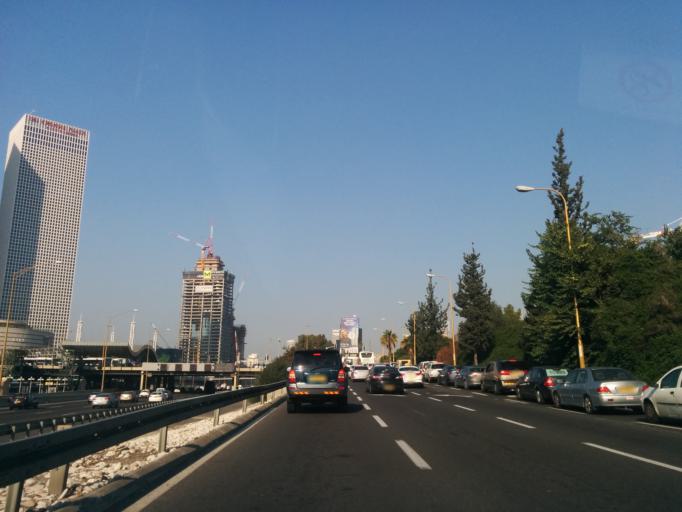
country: IL
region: Tel Aviv
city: Tel Aviv
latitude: 32.0709
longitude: 34.7936
